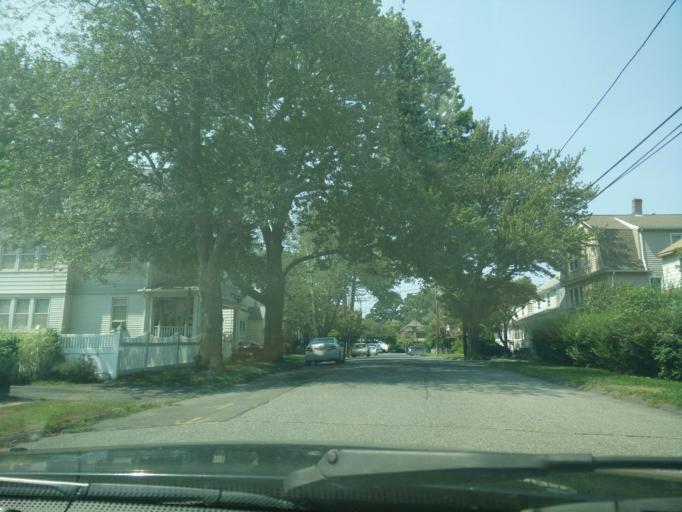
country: US
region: Connecticut
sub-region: Fairfield County
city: Fairfield
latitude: 41.1548
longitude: -73.2389
